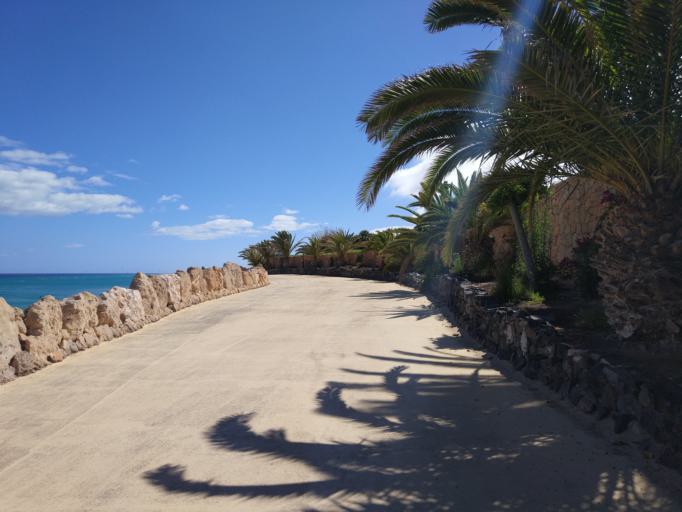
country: ES
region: Canary Islands
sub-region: Provincia de Las Palmas
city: Pajara
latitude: 28.1488
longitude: -14.2317
